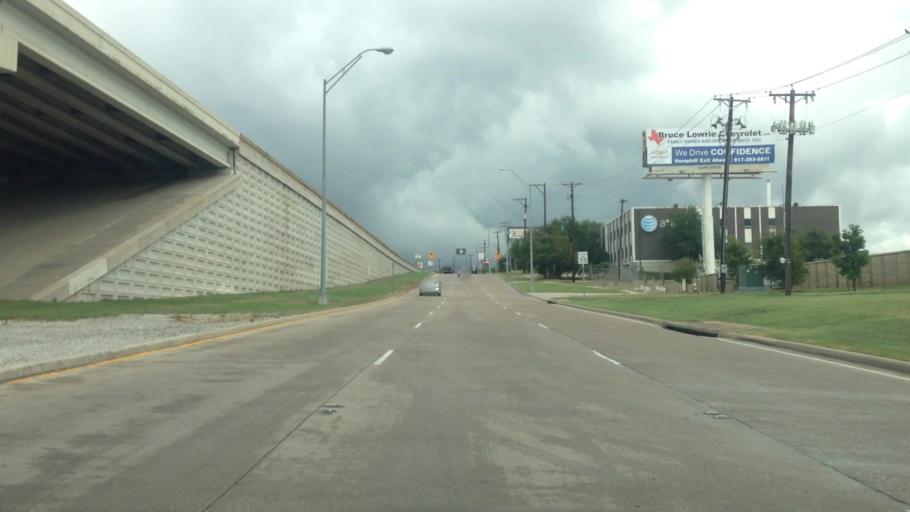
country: US
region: Texas
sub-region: Tarrant County
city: Edgecliff Village
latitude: 32.6745
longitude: -97.3805
